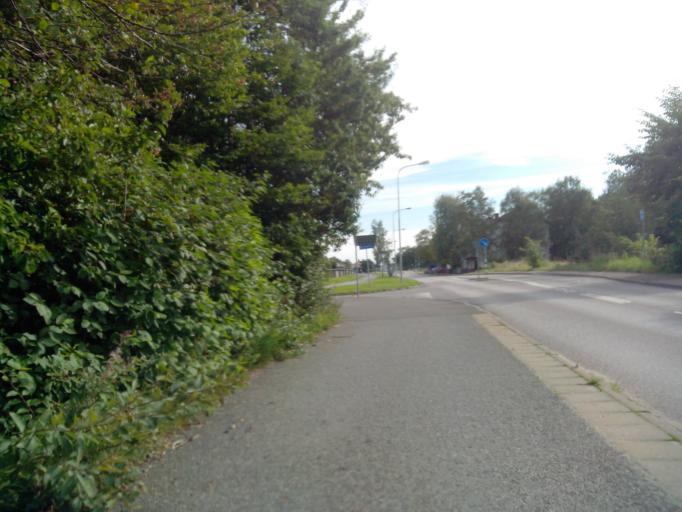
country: SE
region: Vaestra Goetaland
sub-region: Goteborg
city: Goeteborg
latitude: 57.7369
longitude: 11.9567
